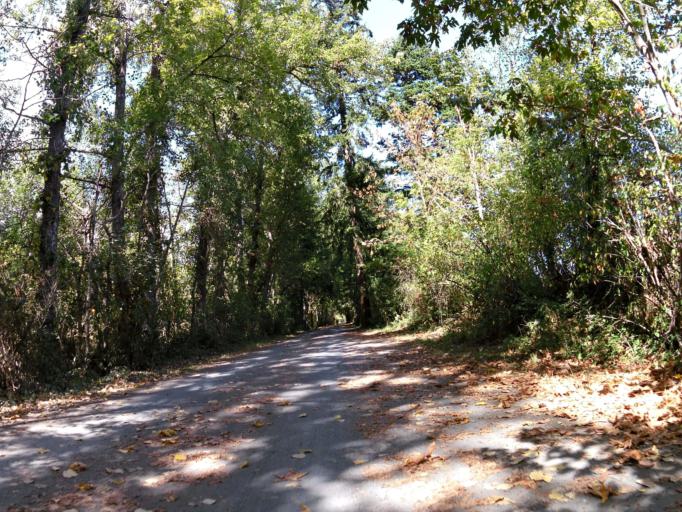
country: CA
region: British Columbia
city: Victoria
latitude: 48.5372
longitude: -123.3792
